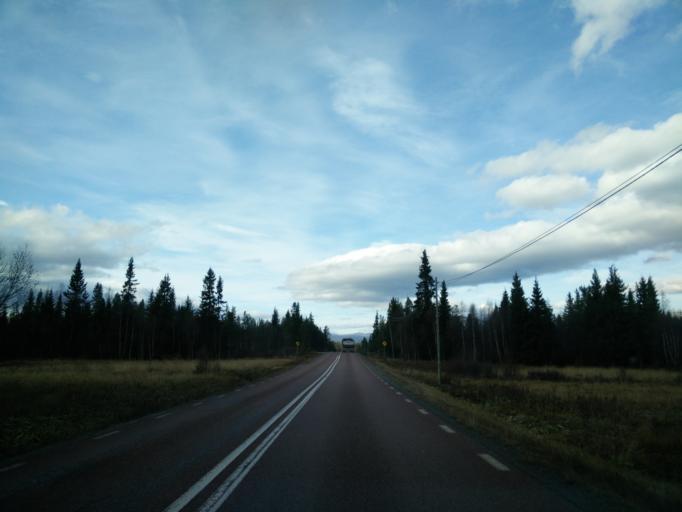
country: NO
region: Hedmark
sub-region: Engerdal
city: Engerdal
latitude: 62.5054
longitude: 12.6180
